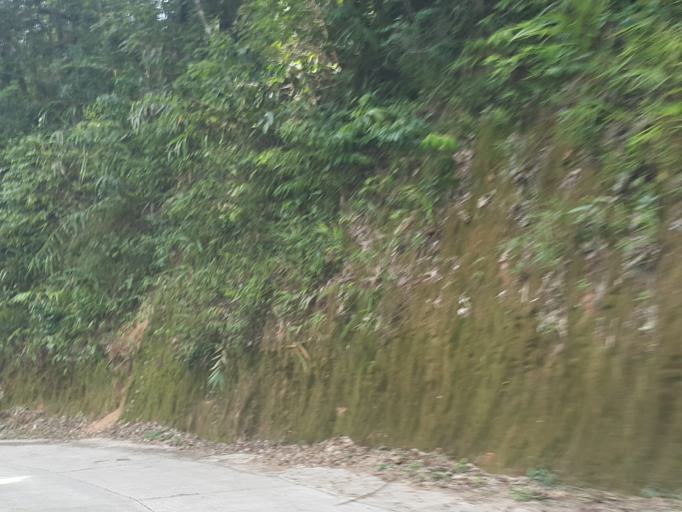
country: TH
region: Chiang Mai
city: Mae On
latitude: 18.8869
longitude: 99.3586
